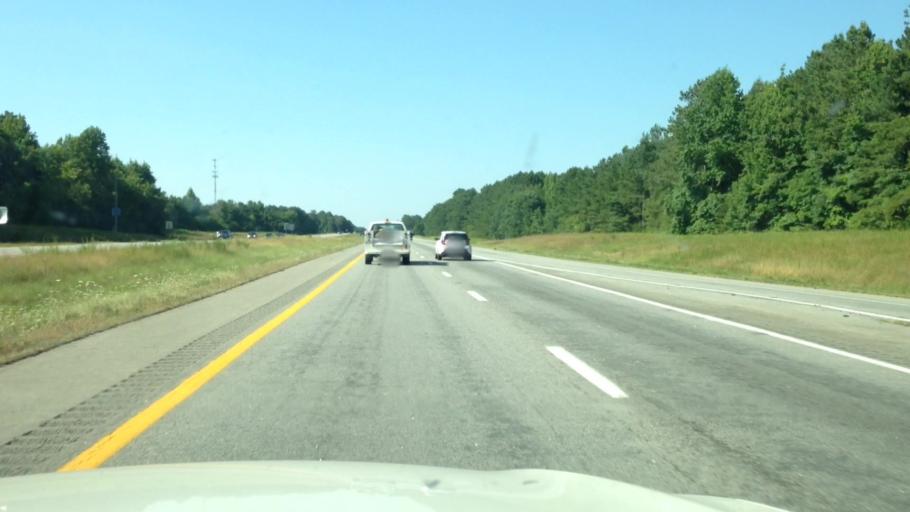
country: US
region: Virginia
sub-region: City of Emporia
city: Emporia
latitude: 36.8081
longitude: -77.4581
